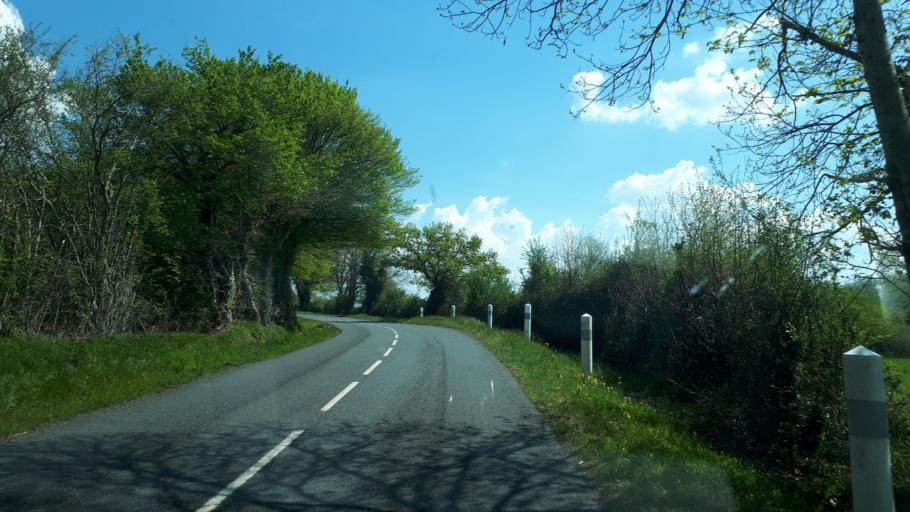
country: FR
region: Centre
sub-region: Departement du Cher
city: Rians
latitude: 47.3000
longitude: 2.6737
